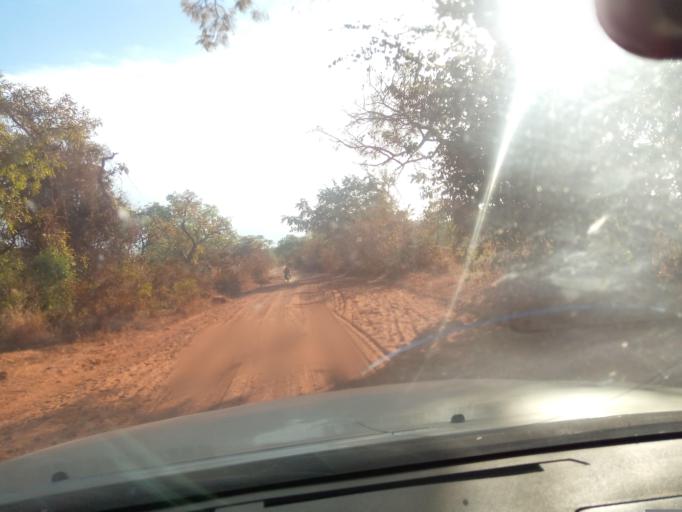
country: ML
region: Sikasso
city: Sikasso
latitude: 11.4222
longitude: -5.5632
